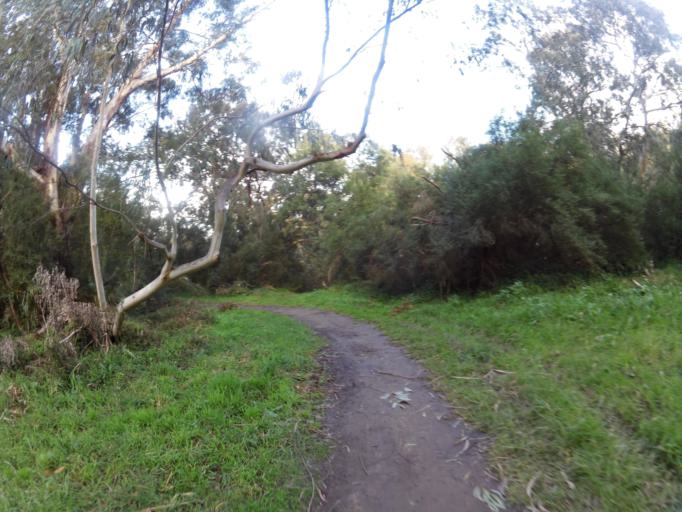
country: AU
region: Victoria
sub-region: Manningham
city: Bulleen
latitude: -37.7527
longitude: 145.0858
